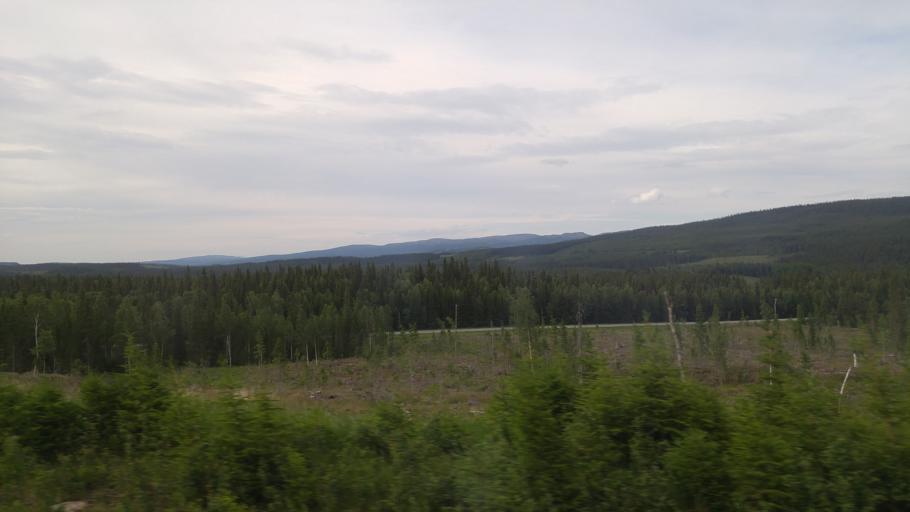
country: SE
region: Jaemtland
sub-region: Are Kommun
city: Are
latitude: 63.3962
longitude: 12.8121
